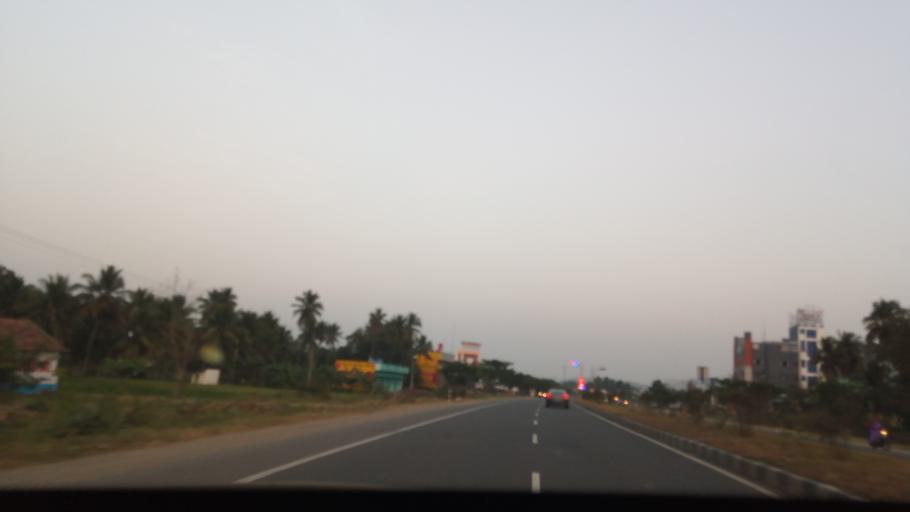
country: IN
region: Tamil Nadu
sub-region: Salem
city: Salem
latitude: 11.6668
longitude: 78.2609
